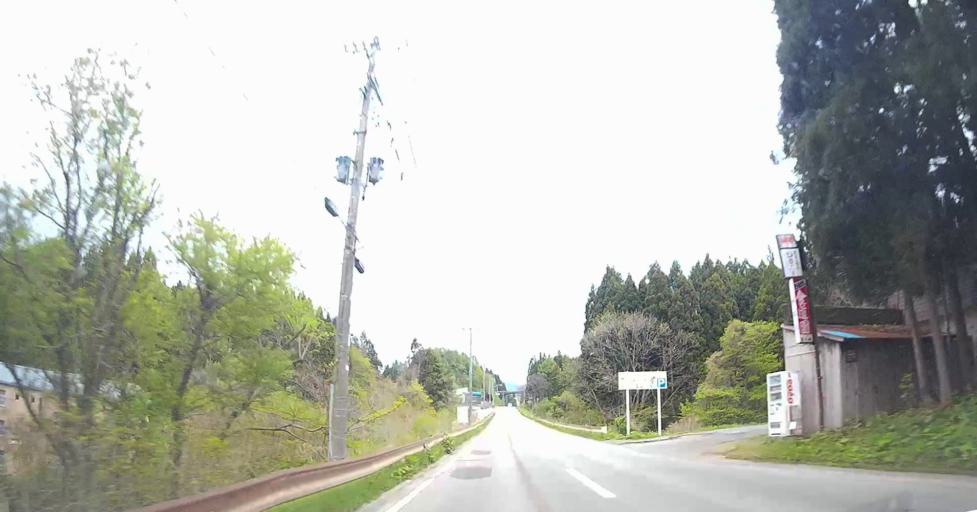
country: JP
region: Aomori
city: Goshogawara
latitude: 41.1775
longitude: 140.4815
